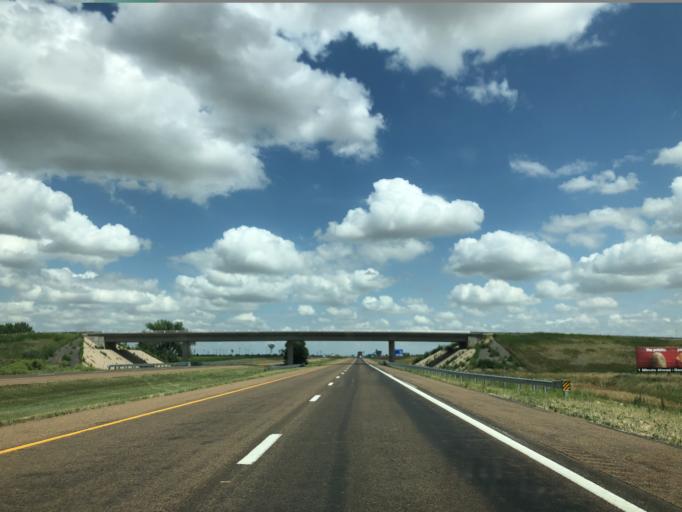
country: US
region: Kansas
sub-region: Sherman County
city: Goodland
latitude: 39.3291
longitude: -101.7469
